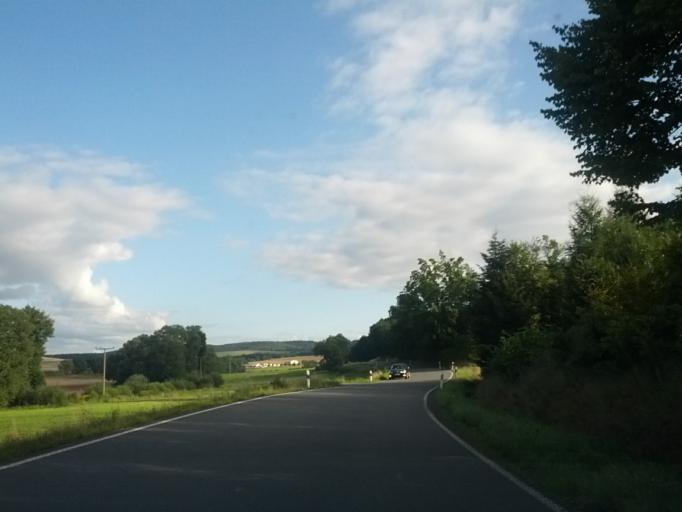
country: DE
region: Thuringia
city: Lauchroden
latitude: 50.9619
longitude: 10.1634
